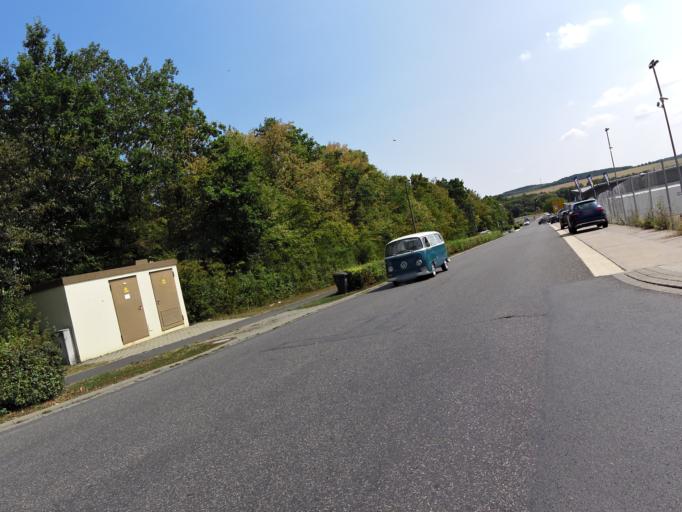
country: DE
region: Bavaria
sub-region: Regierungsbezirk Unterfranken
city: Estenfeld
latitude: 49.8420
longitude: 10.0156
